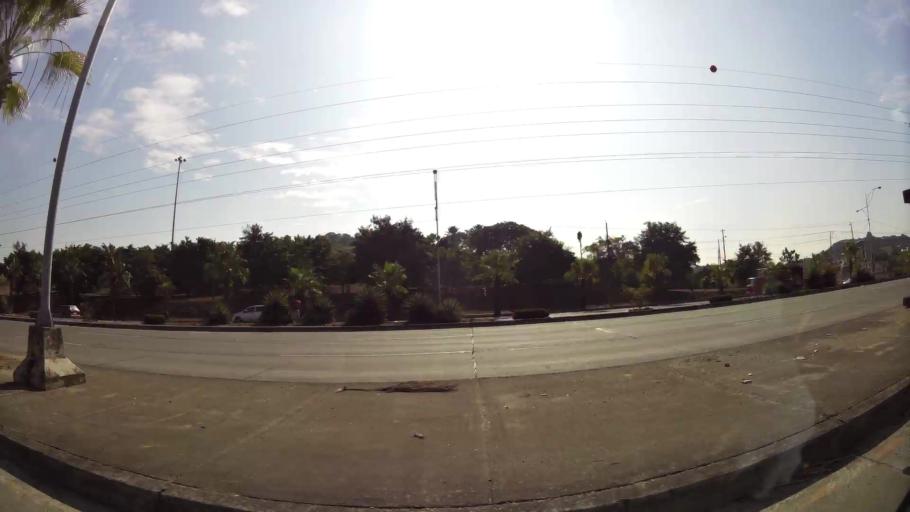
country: EC
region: Guayas
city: Eloy Alfaro
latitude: -2.0778
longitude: -79.9169
